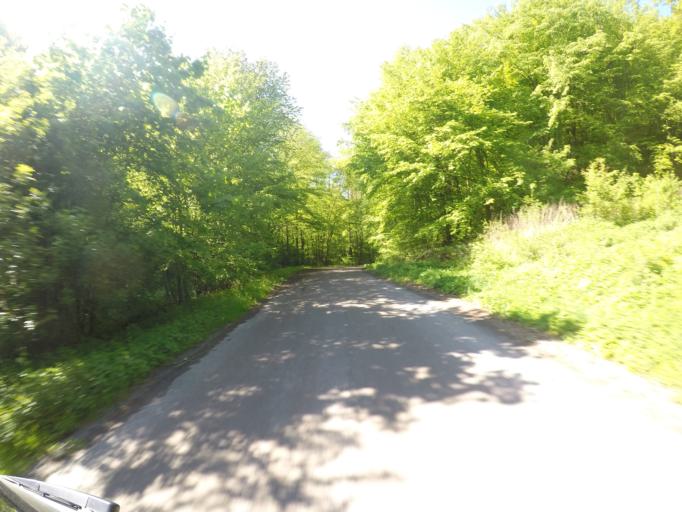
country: SK
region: Banskobystricky
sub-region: Okres Banska Bystrica
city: Zvolen
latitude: 48.5810
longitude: 19.0048
